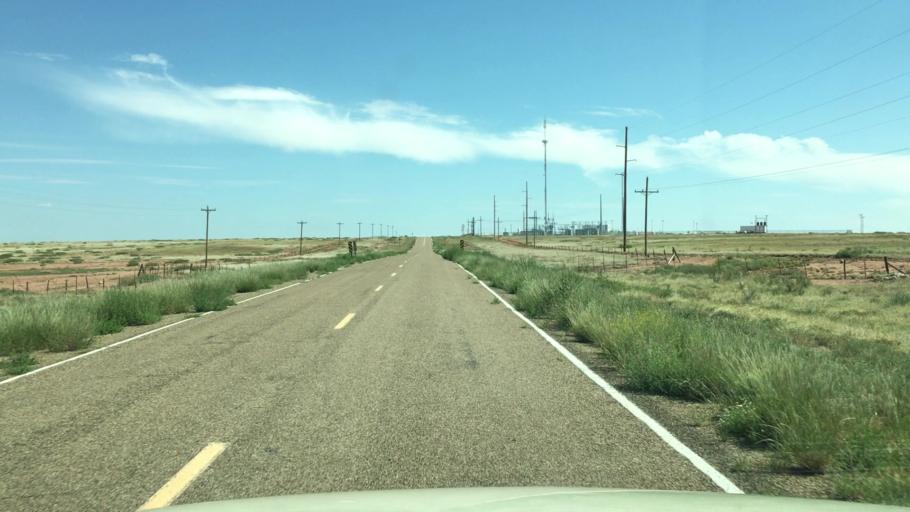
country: US
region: New Mexico
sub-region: Chaves County
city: Roswell
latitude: 33.9595
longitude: -104.5843
